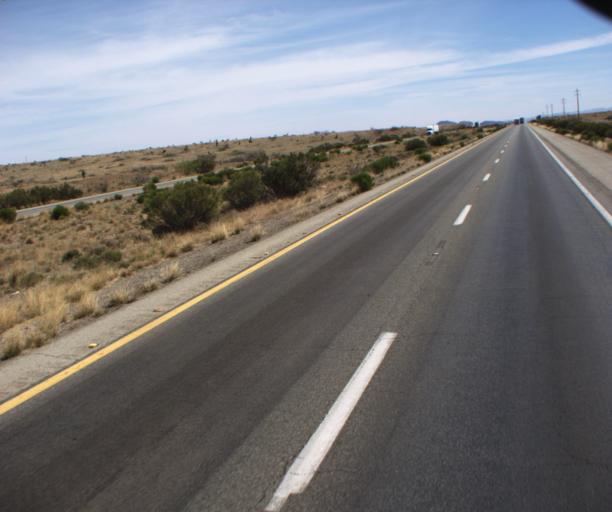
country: US
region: Arizona
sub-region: Cochise County
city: Willcox
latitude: 32.3511
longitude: -109.7280
